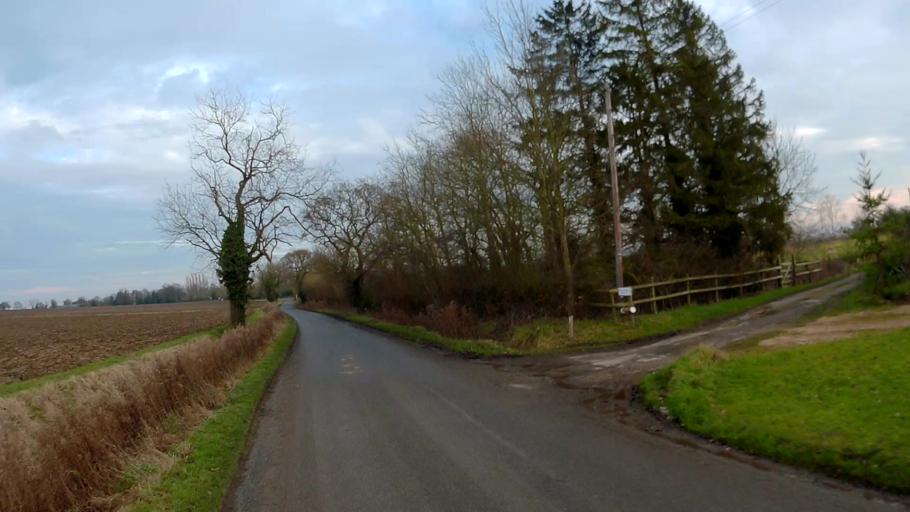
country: GB
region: England
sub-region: Lincolnshire
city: Bourne
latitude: 52.8312
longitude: -0.4194
